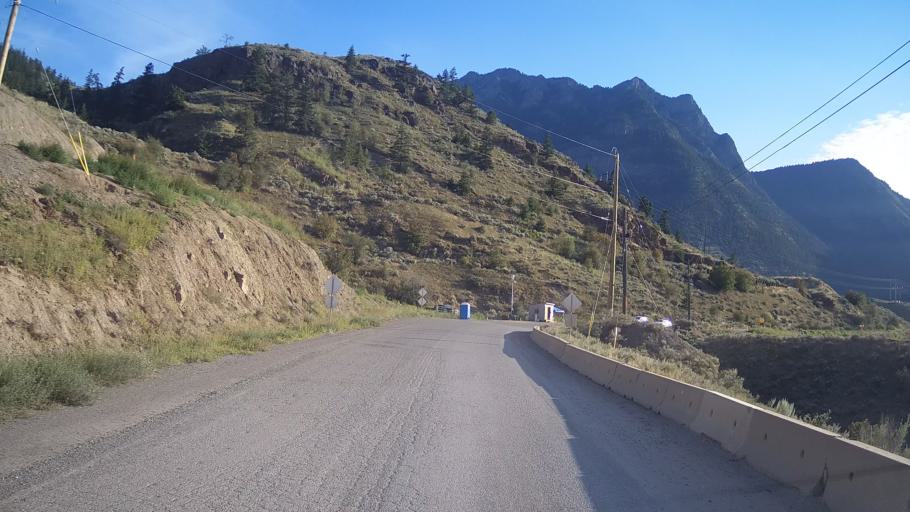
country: CA
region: British Columbia
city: Lillooet
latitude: 50.7464
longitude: -121.8519
